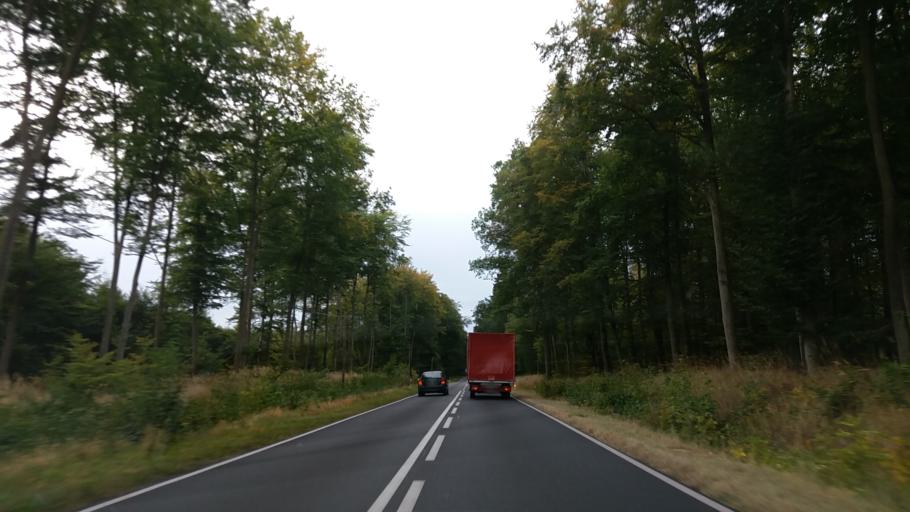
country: PL
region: West Pomeranian Voivodeship
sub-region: Powiat mysliborski
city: Barlinek
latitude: 52.9405
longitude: 15.1905
